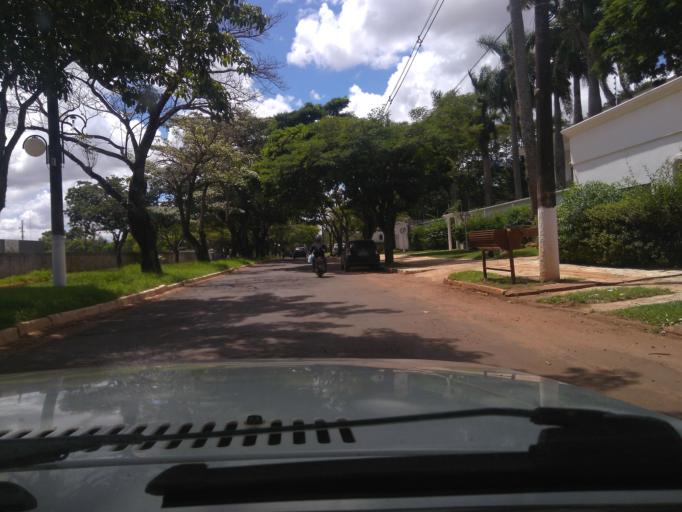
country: BR
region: Mato Grosso do Sul
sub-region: Ponta Pora
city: Ponta Pora
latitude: -22.5274
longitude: -55.7272
